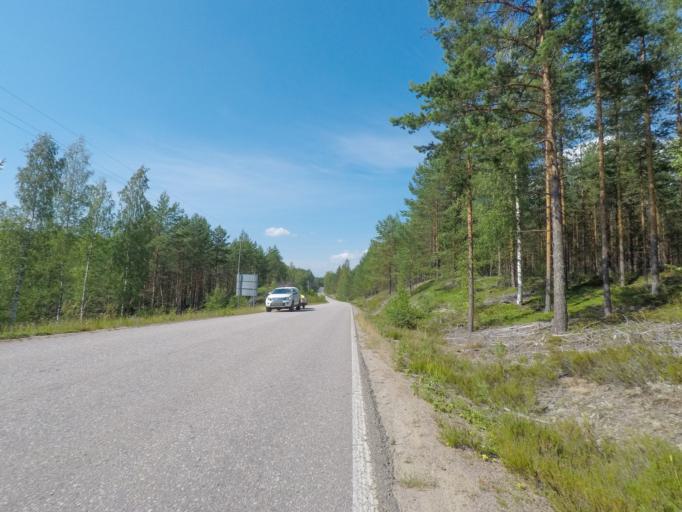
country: FI
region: Southern Savonia
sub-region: Mikkeli
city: Puumala
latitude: 61.4610
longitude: 28.1758
